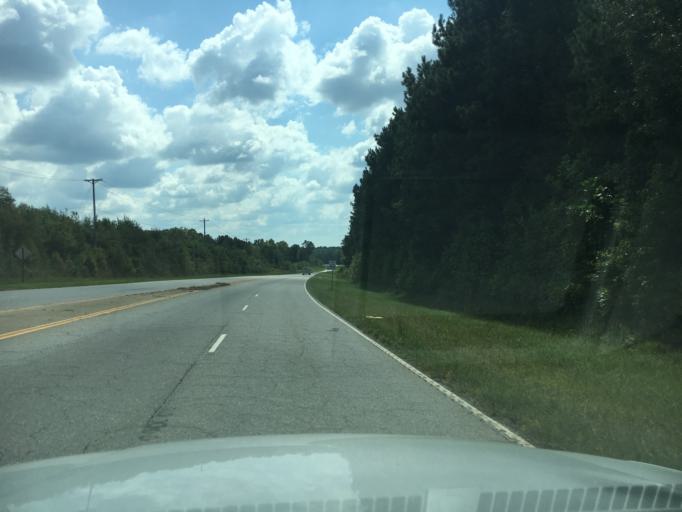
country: US
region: South Carolina
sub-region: Greenwood County
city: Greenwood
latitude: 34.1736
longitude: -82.1828
